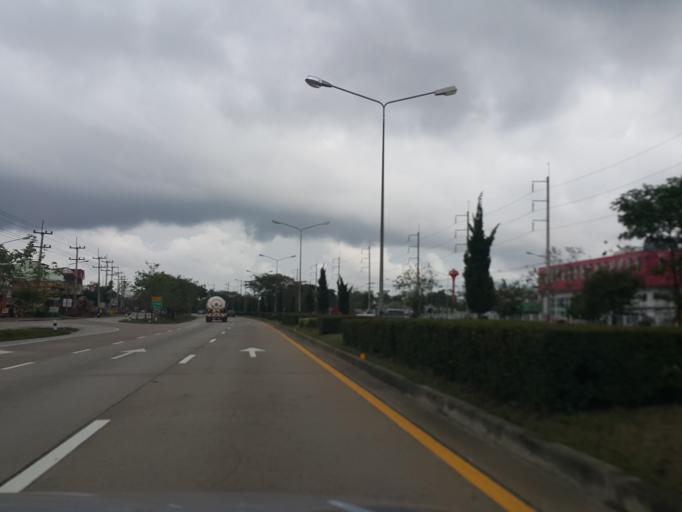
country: TH
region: Lampang
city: Lampang
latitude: 18.2781
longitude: 99.4540
